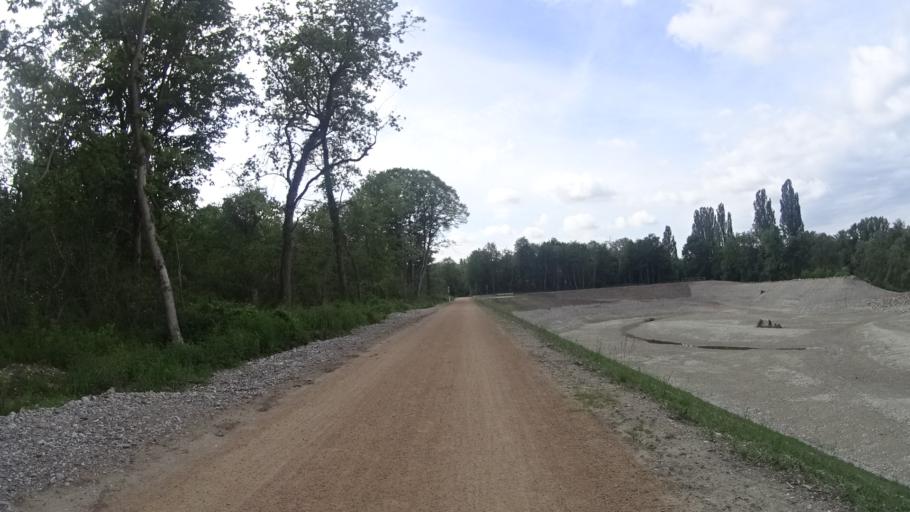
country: DE
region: Baden-Wuerttemberg
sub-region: Freiburg Region
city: Bad Bellingen
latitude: 47.7464
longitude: 7.5472
